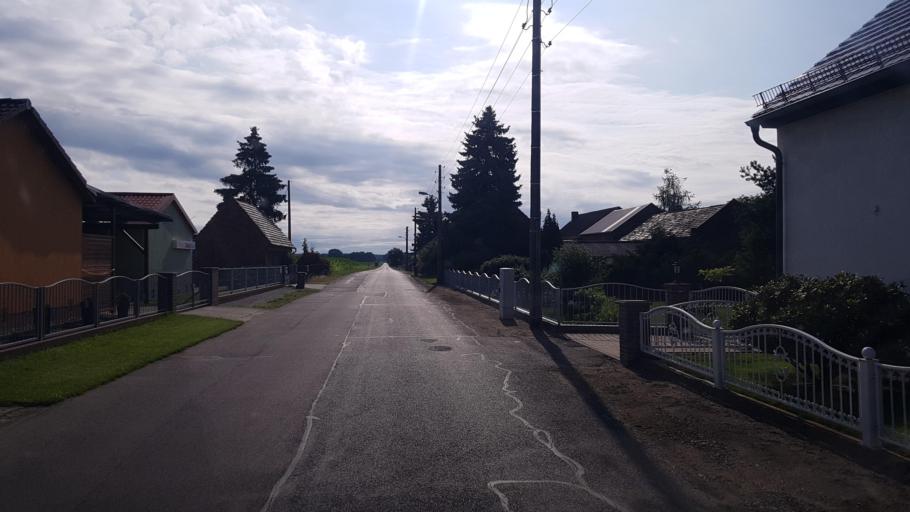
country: DE
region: Brandenburg
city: Grossraschen
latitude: 51.5880
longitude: 14.0389
